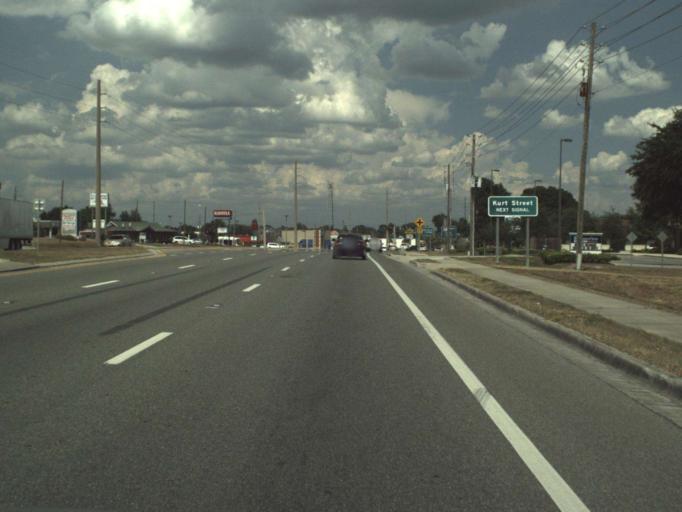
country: US
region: Florida
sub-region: Lake County
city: Eustis
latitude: 28.8225
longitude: -81.6942
